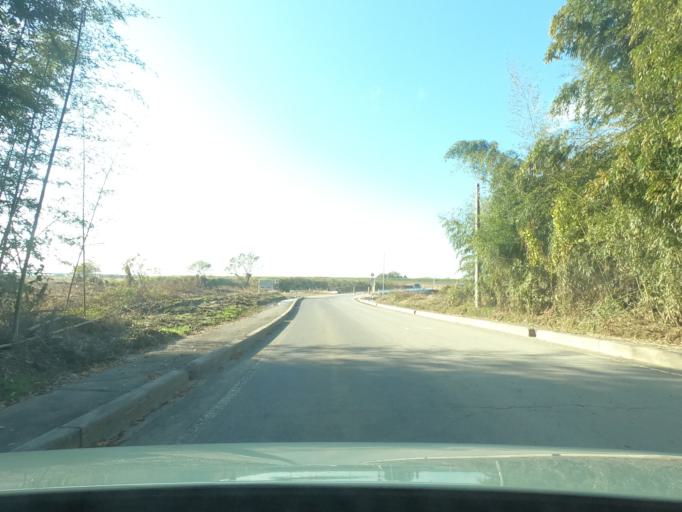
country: JP
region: Ibaraki
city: Koga
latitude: 36.2452
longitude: 139.7348
